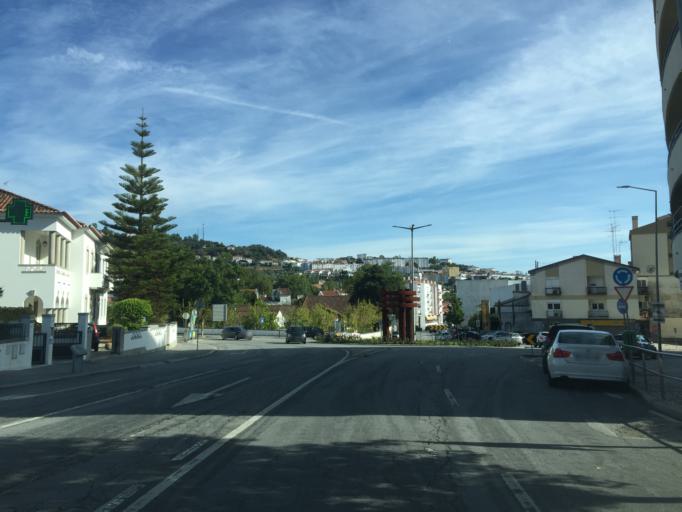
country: PT
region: Portalegre
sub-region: Portalegre
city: Portalegre
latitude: 39.3001
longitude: -7.4321
